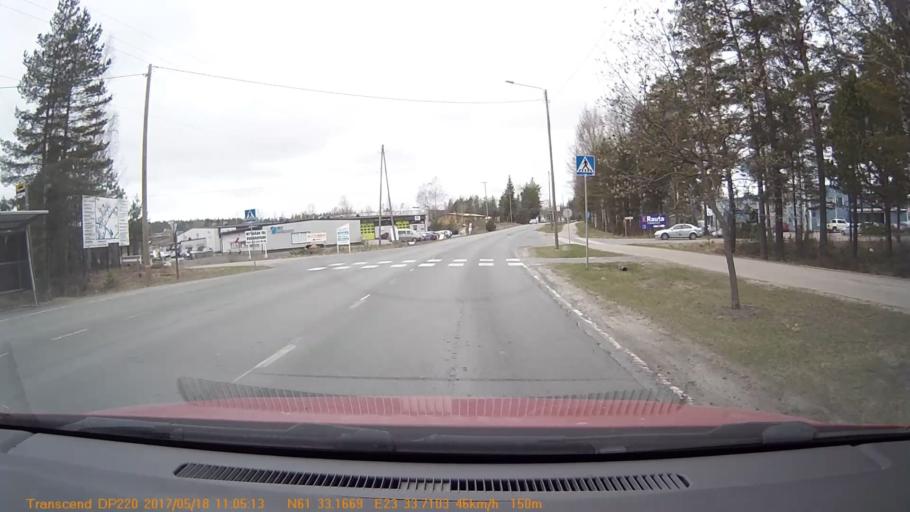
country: FI
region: Pirkanmaa
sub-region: Tampere
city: Yloejaervi
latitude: 61.5528
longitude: 23.5621
